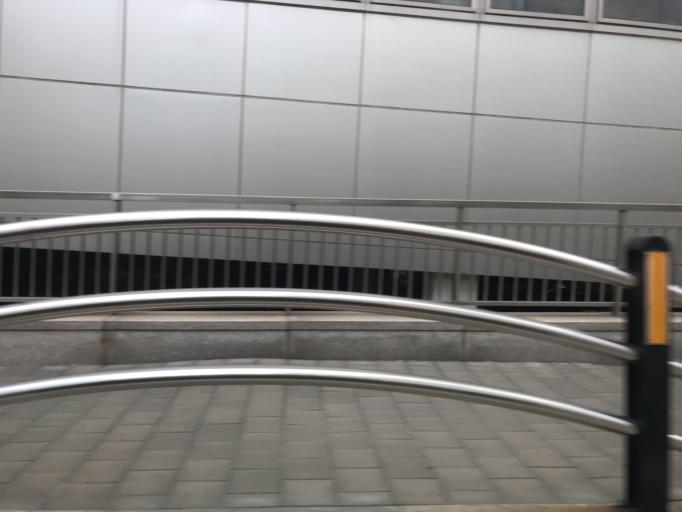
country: KR
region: Seoul
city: Seoul
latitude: 37.5637
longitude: 126.9415
